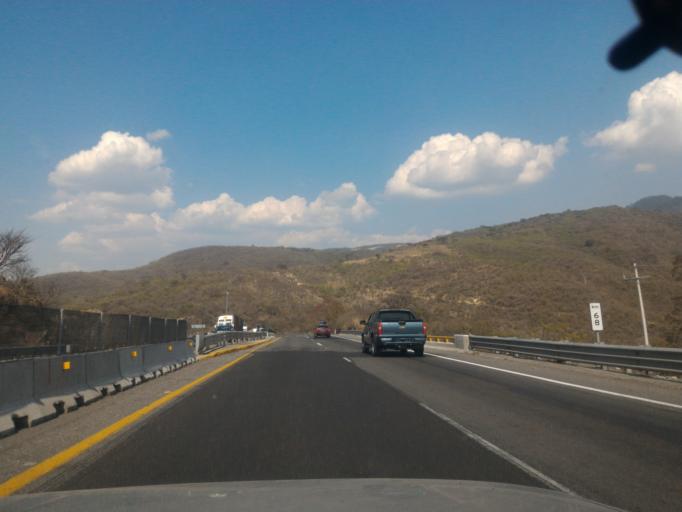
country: MX
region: Jalisco
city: Usmajac
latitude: 19.8529
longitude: -103.5071
